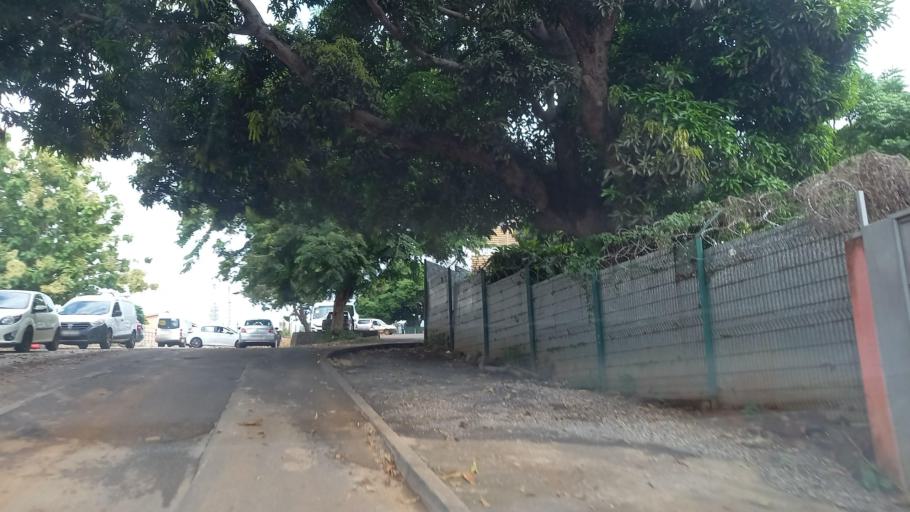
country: YT
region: Sada
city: Sada
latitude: -12.8486
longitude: 45.1051
